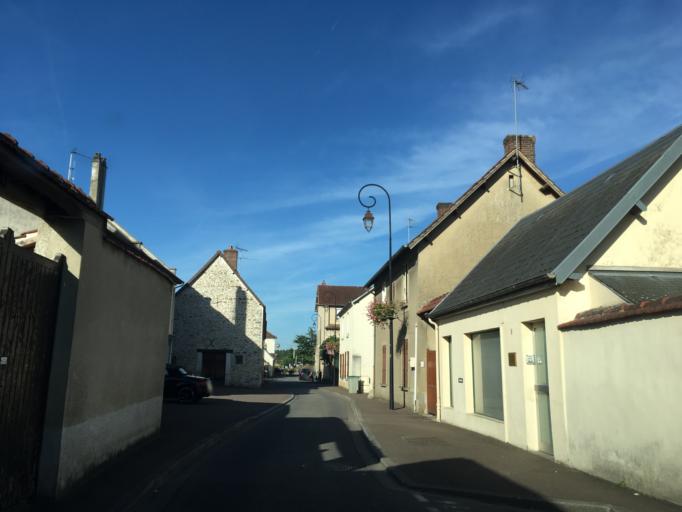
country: FR
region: Haute-Normandie
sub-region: Departement de l'Eure
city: Gasny
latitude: 49.0914
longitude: 1.6025
